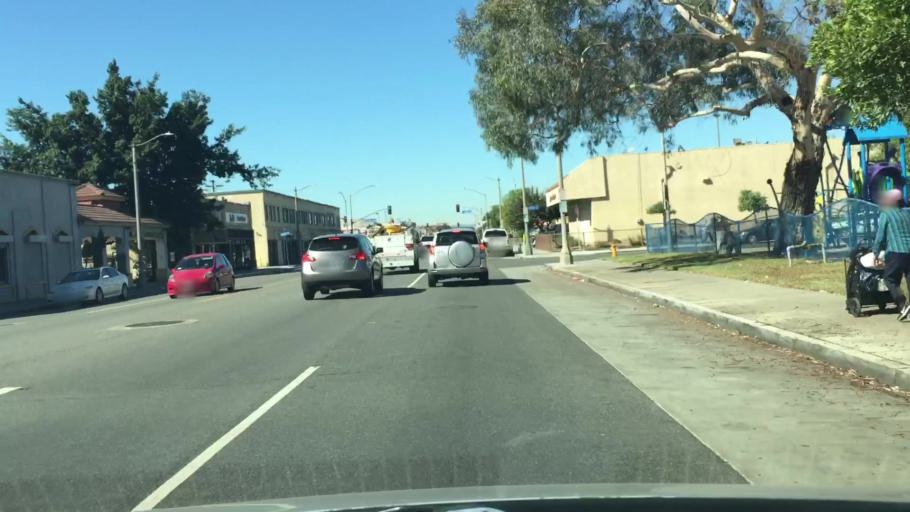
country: US
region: California
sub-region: Los Angeles County
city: Long Beach
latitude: 33.7827
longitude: -118.1748
